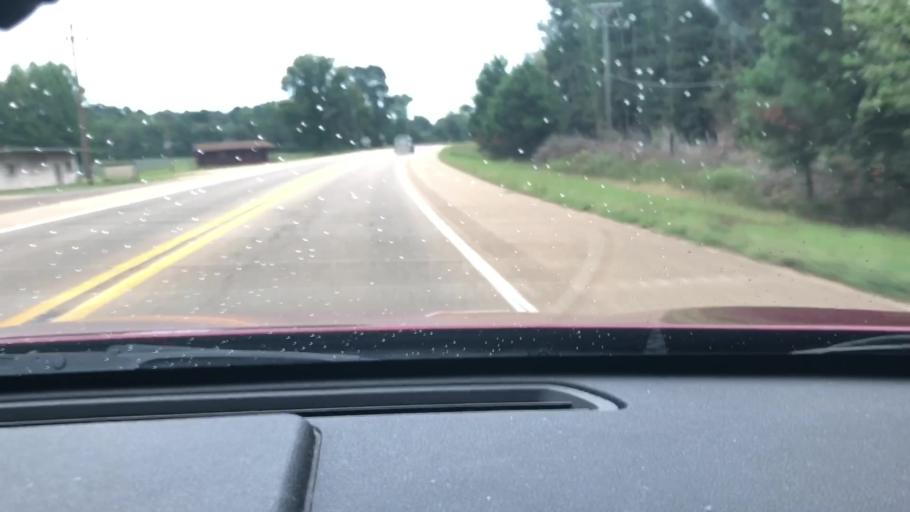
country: US
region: Arkansas
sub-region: Lafayette County
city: Stamps
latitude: 33.3670
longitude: -93.5138
